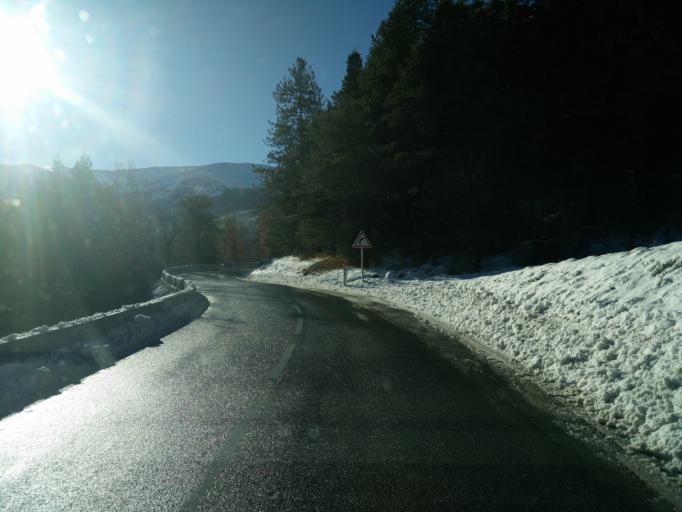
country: FR
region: Provence-Alpes-Cote d'Azur
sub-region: Departement des Alpes-de-Haute-Provence
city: Annot
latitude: 43.9355
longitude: 6.6353
